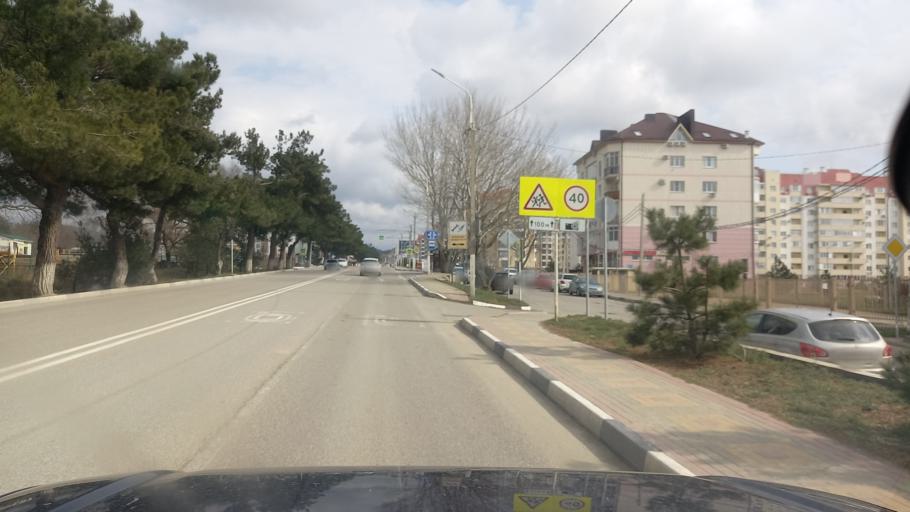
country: RU
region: Krasnodarskiy
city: Gelendzhik
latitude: 44.5584
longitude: 38.1002
